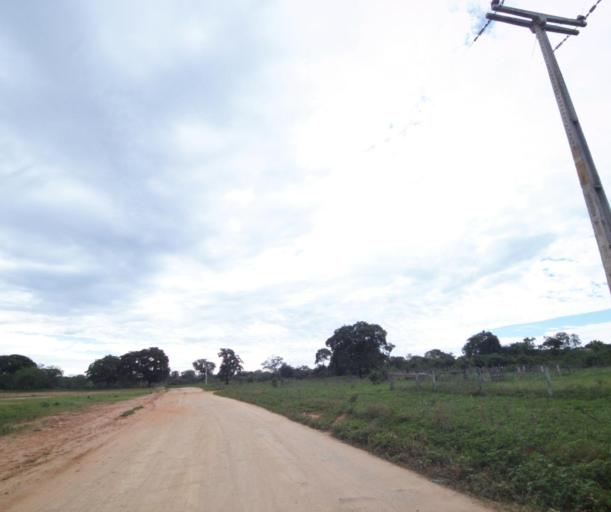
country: BR
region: Bahia
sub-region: Carinhanha
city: Carinhanha
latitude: -14.1802
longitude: -44.5252
